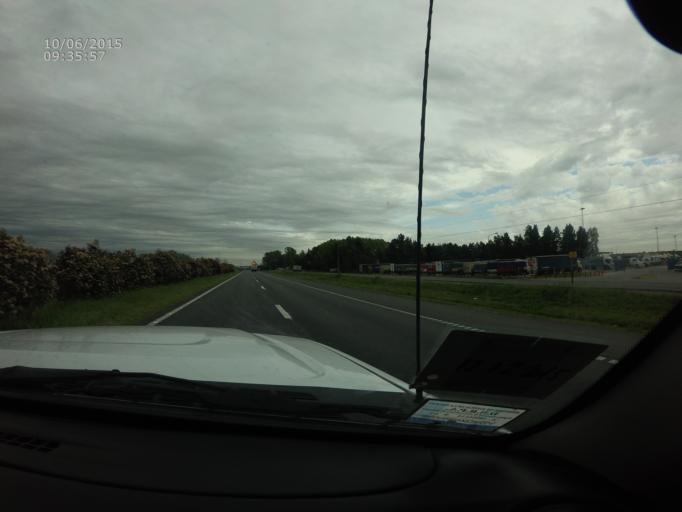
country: AR
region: Buenos Aires
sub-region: Partido de Zarate
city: Zarate
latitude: -34.1029
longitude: -59.1451
